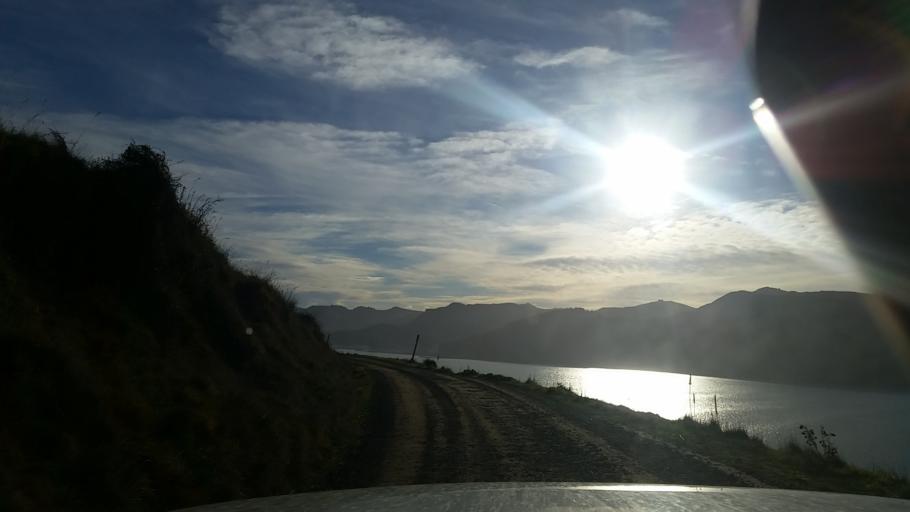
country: NZ
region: Canterbury
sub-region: Christchurch City
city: Christchurch
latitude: -43.6205
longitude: 172.7680
